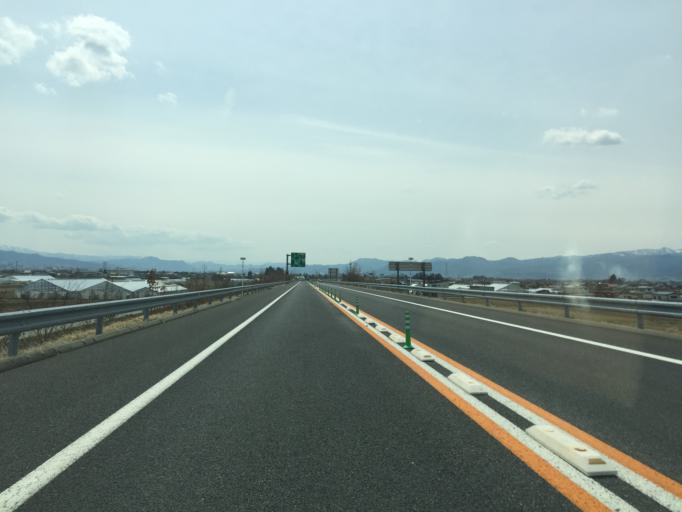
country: JP
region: Yamagata
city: Tendo
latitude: 38.3247
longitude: 140.3267
